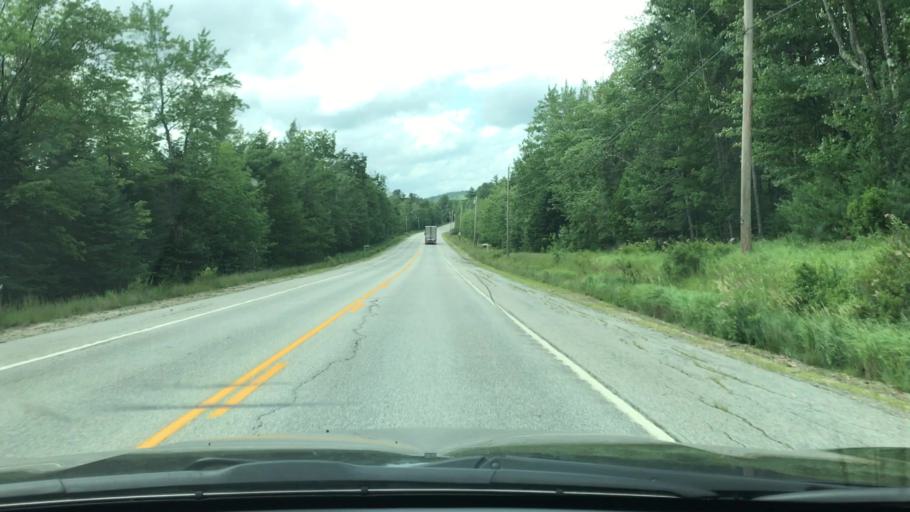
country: US
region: Maine
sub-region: Oxford County
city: West Paris
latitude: 44.3697
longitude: -70.6009
